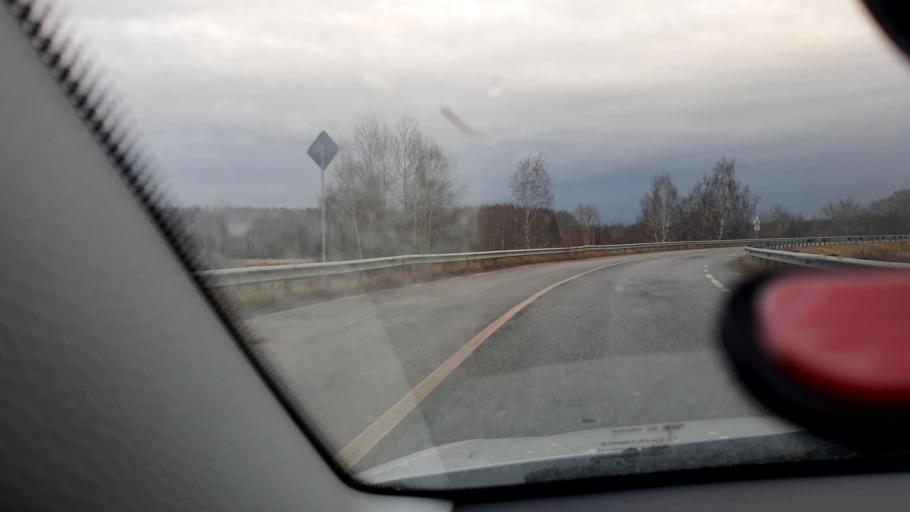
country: RU
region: Bashkortostan
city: Mikhaylovka
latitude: 54.7074
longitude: 55.8544
